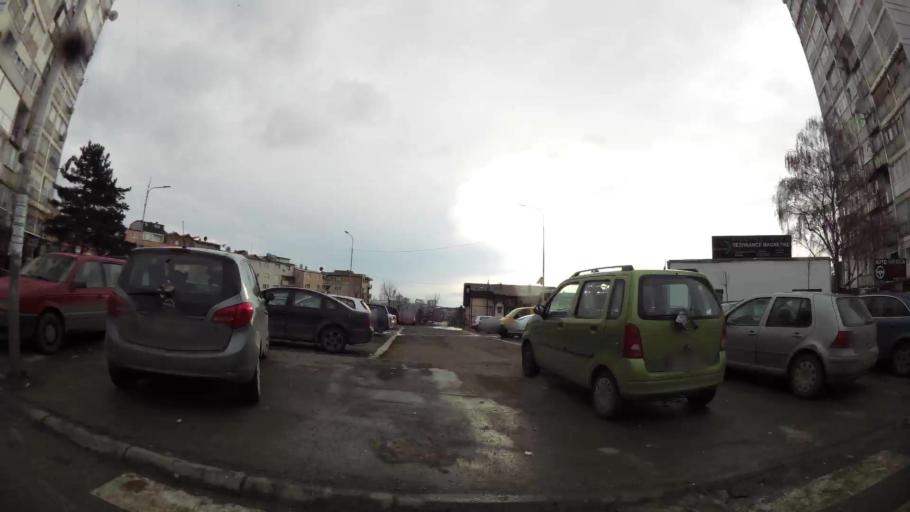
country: XK
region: Pristina
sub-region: Komuna e Prishtines
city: Pristina
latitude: 42.6506
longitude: 21.1625
